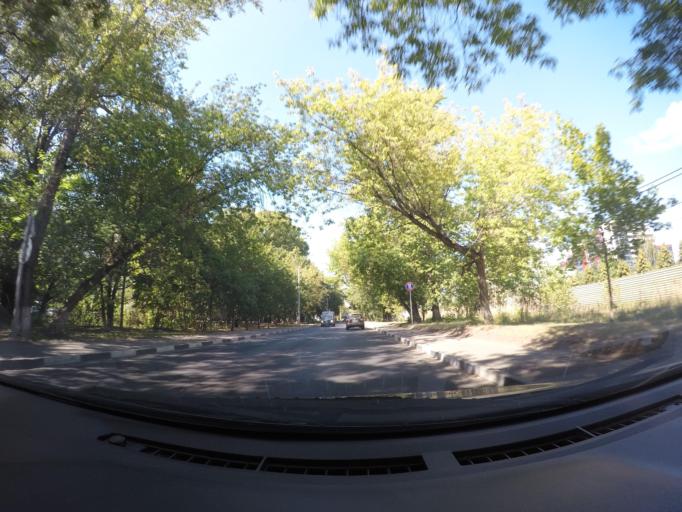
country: RU
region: Moskovskaya
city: Tomilino
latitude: 55.6614
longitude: 37.9360
